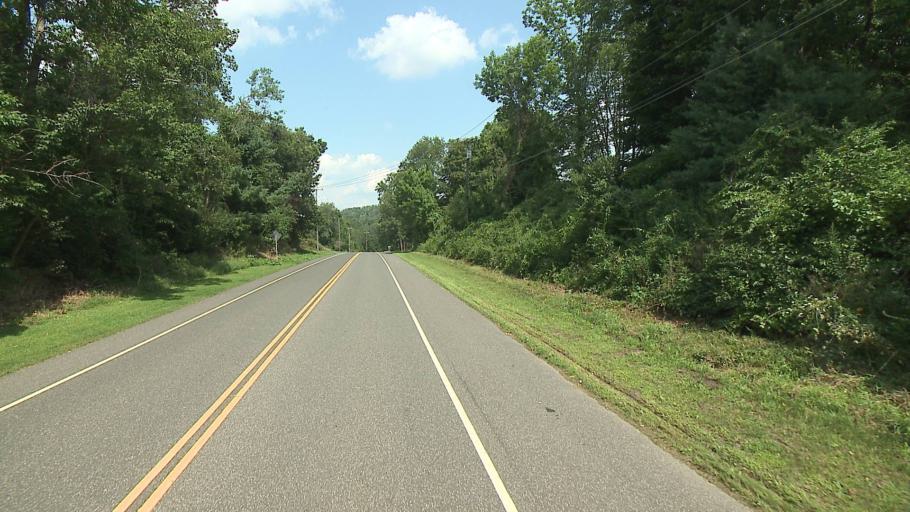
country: US
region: Connecticut
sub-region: Litchfield County
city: Bethlehem Village
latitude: 41.6769
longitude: -73.2570
